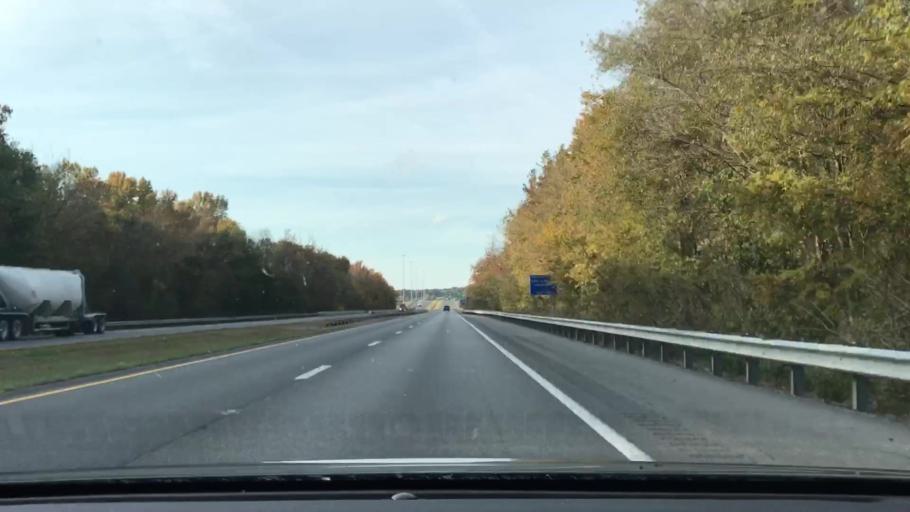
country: US
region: Kentucky
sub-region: Marshall County
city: Benton
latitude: 36.8803
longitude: -88.3583
